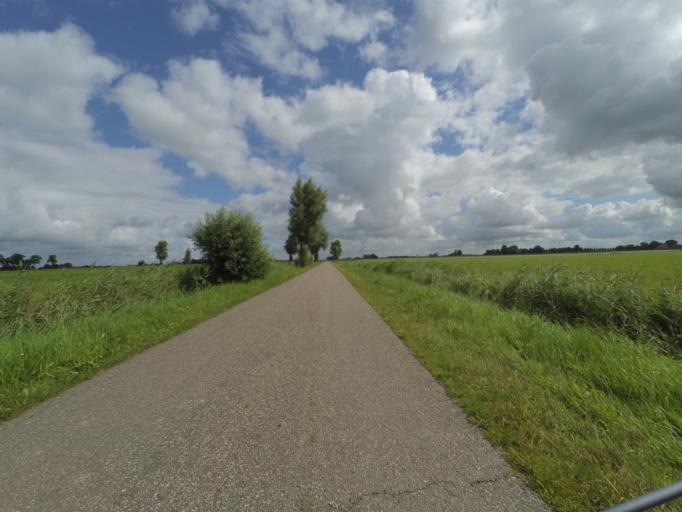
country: NL
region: Friesland
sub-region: Gemeente Kollumerland en Nieuwkruisland
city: Kollum
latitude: 53.2707
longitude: 6.1771
